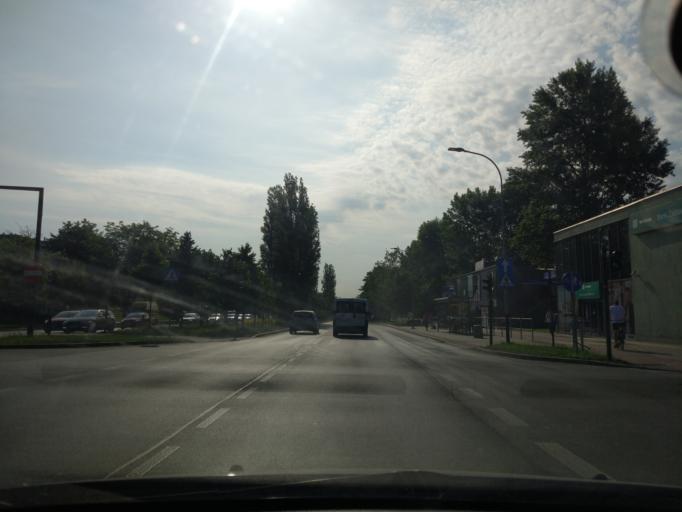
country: PL
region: Lesser Poland Voivodeship
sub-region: Powiat krakowski
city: Michalowice
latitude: 50.0858
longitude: 20.0133
